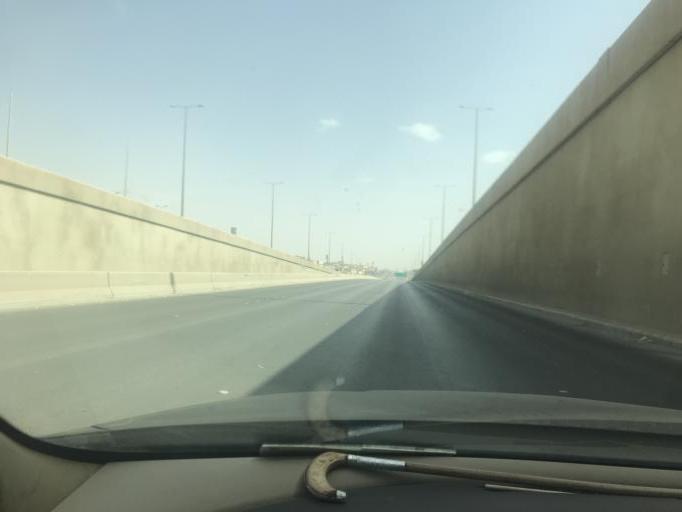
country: SA
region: Ar Riyad
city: Riyadh
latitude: 24.7791
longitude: 46.7072
